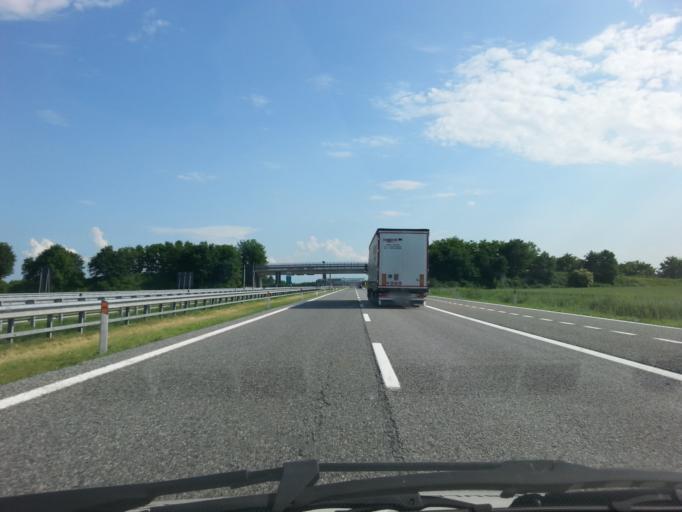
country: IT
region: Piedmont
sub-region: Provincia di Torino
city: Carmagnola
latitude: 44.8461
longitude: 7.7488
